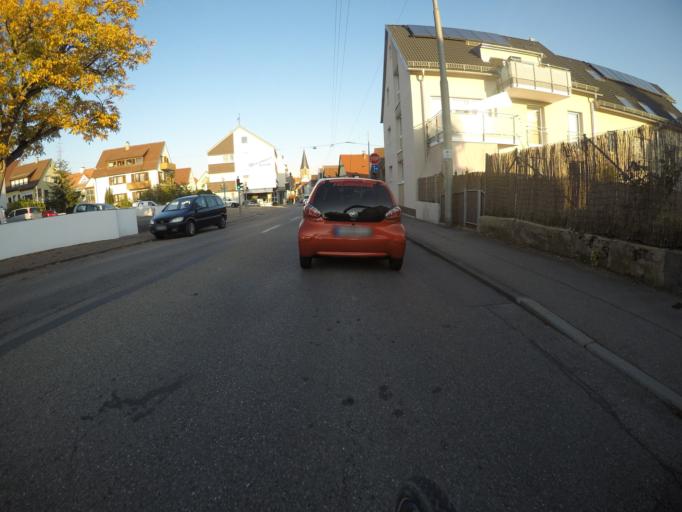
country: DE
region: Baden-Wuerttemberg
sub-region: Regierungsbezirk Stuttgart
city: Steinenbronn
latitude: 48.7325
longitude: 9.1066
